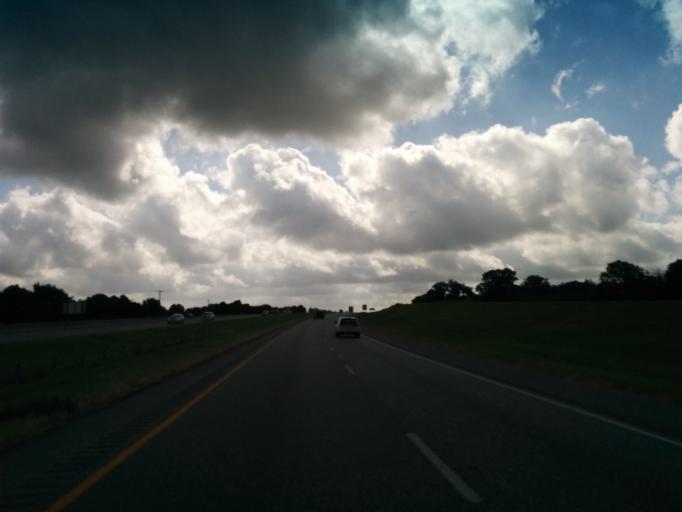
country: US
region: Texas
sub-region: Caldwell County
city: Luling
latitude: 29.6541
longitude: -97.5813
